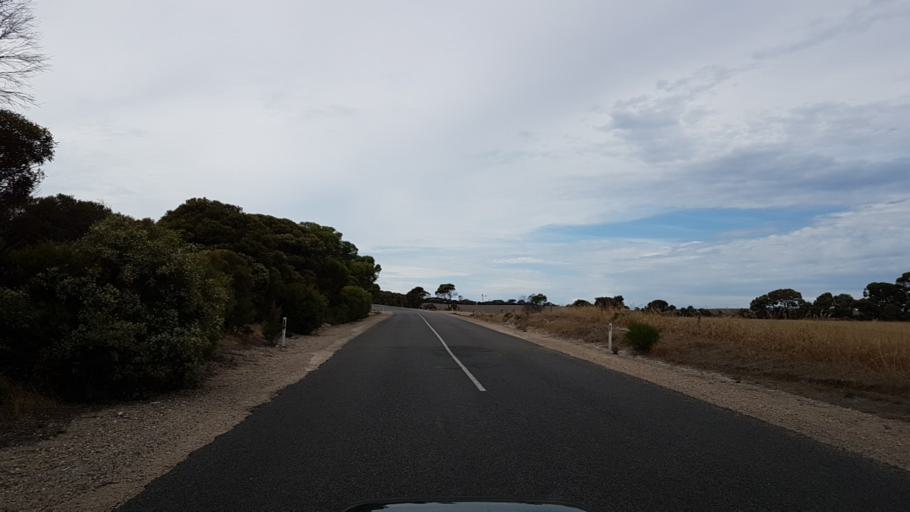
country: AU
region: South Australia
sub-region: Yorke Peninsula
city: Honiton
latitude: -34.9689
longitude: 137.1103
